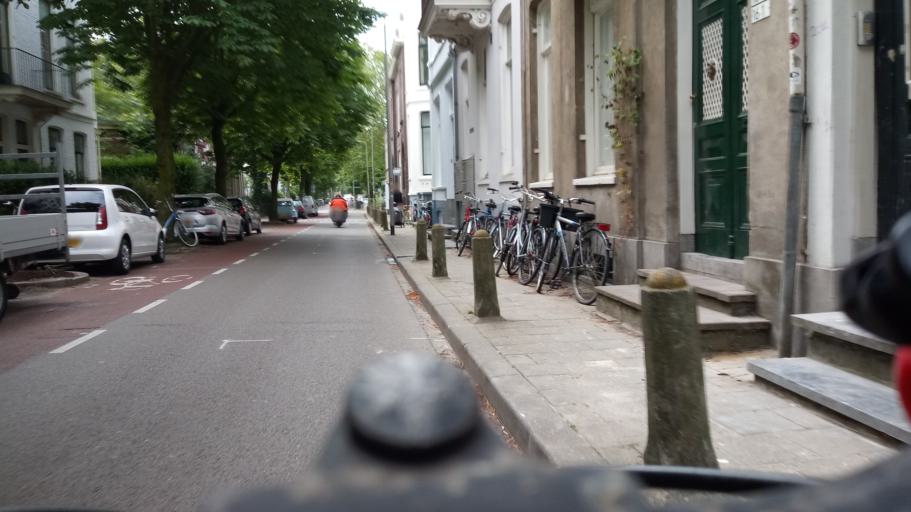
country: NL
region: Gelderland
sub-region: Gemeente Arnhem
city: Arnhem
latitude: 51.9824
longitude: 5.9189
